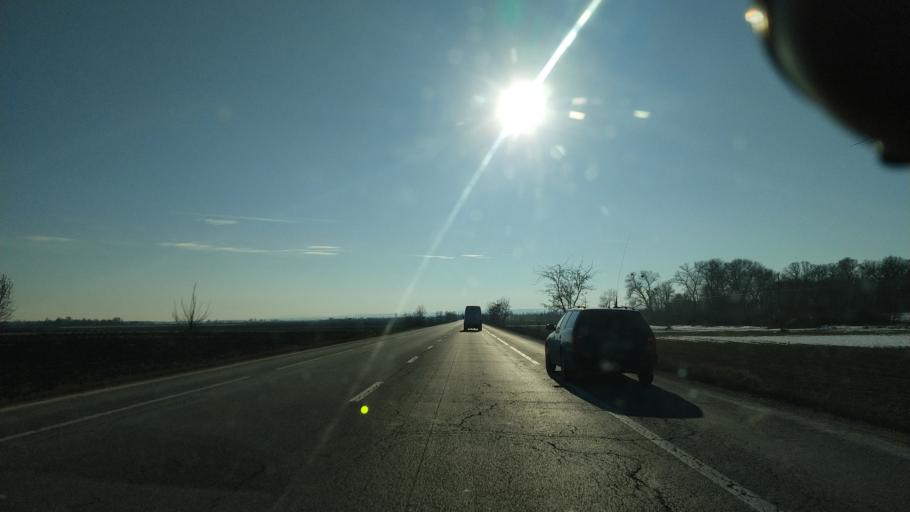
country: RO
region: Neamt
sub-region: Municipiul Roman
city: Roman
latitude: 46.8764
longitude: 26.8983
